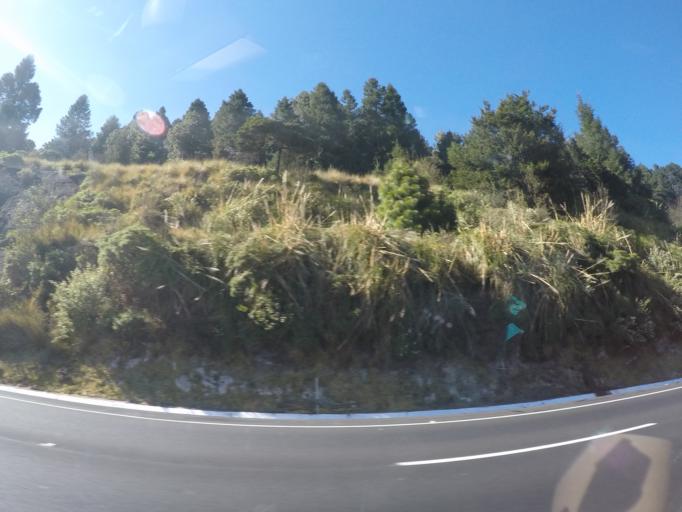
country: MX
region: Mexico City
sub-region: Cuajimalpa de Morelos
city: San Lorenzo Acopilco
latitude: 19.3077
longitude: -99.3444
